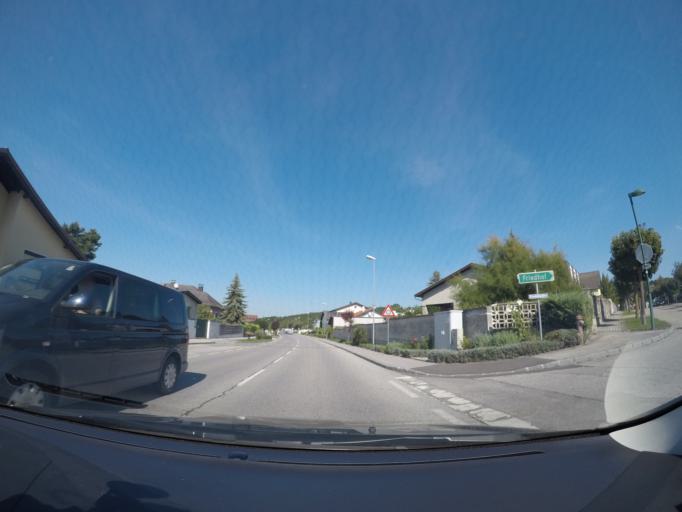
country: AT
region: Lower Austria
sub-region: Politischer Bezirk Bruck an der Leitha
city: Hof am Leithaberge
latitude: 47.9469
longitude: 16.5827
